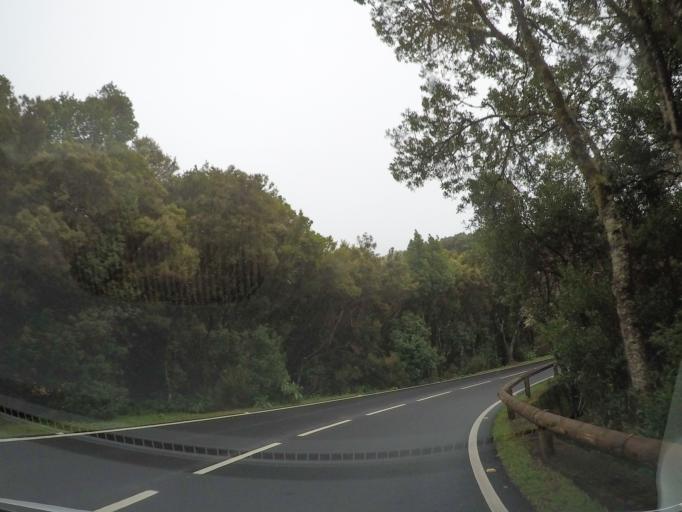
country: ES
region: Canary Islands
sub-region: Provincia de Santa Cruz de Tenerife
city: Vallehermosa
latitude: 28.1275
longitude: -17.2629
